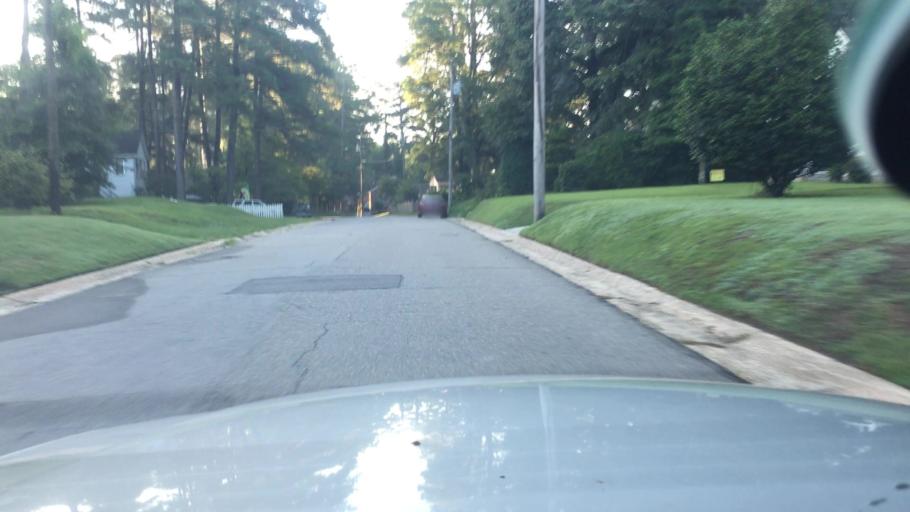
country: US
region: North Carolina
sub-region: Cumberland County
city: Fayetteville
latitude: 35.0620
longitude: -78.9148
